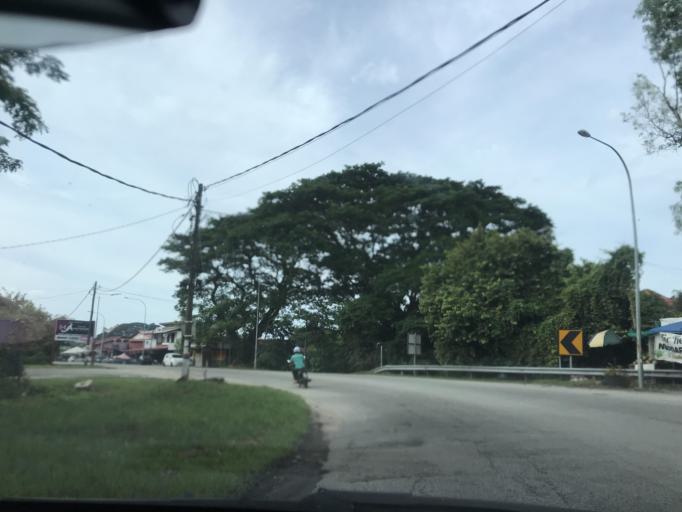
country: MY
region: Kelantan
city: Kota Bharu
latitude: 6.1025
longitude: 102.2349
